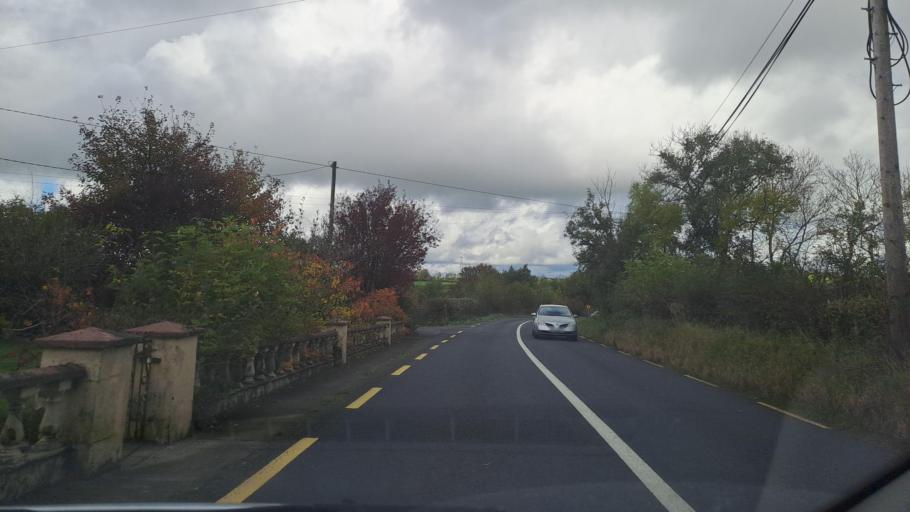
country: IE
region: Ulster
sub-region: An Cabhan
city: Bailieborough
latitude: 53.8845
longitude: -6.9641
